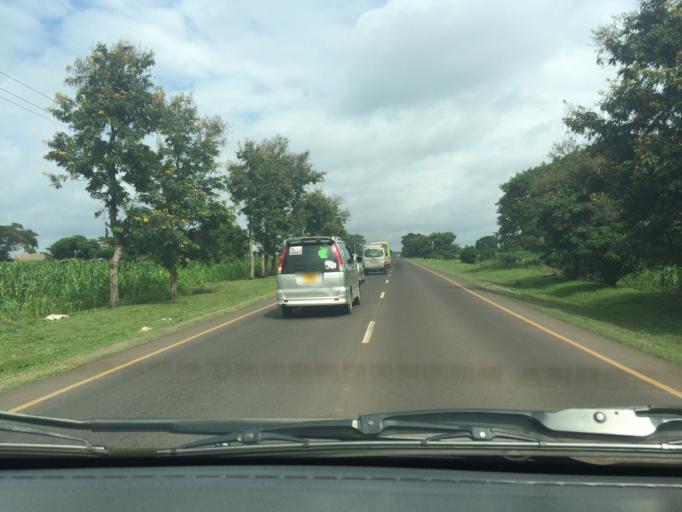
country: TZ
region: Arusha
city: Usa River
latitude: -3.3881
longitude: 36.9525
